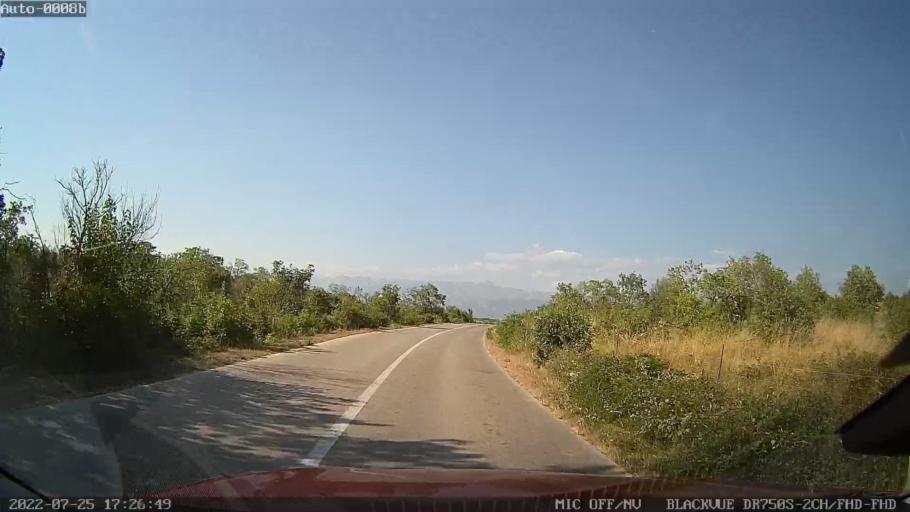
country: HR
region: Zadarska
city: Pridraga
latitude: 44.1372
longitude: 15.5023
